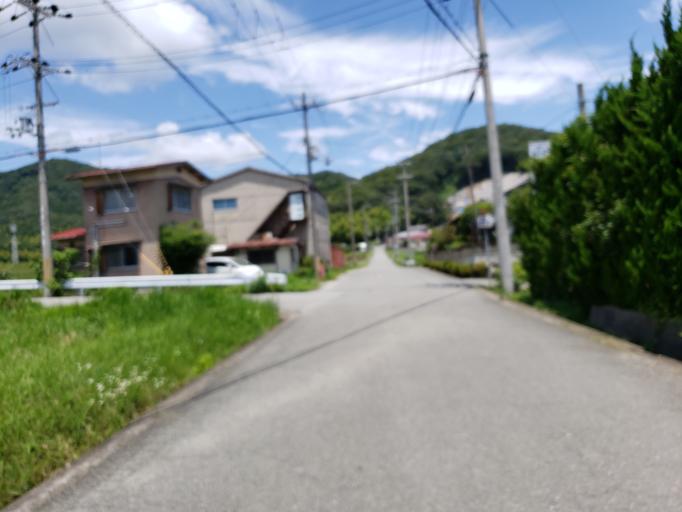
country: JP
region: Hyogo
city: Kakogawacho-honmachi
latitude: 34.8247
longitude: 134.8118
